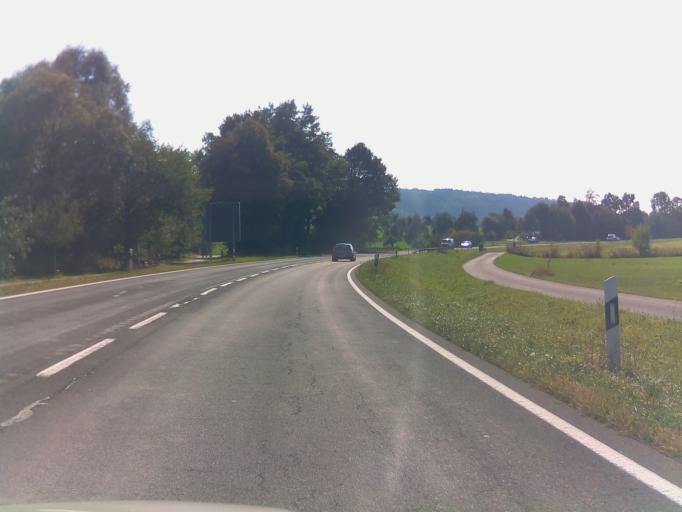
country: DE
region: Bavaria
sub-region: Regierungsbezirk Unterfranken
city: Untermerzbach
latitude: 50.1304
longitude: 10.8919
